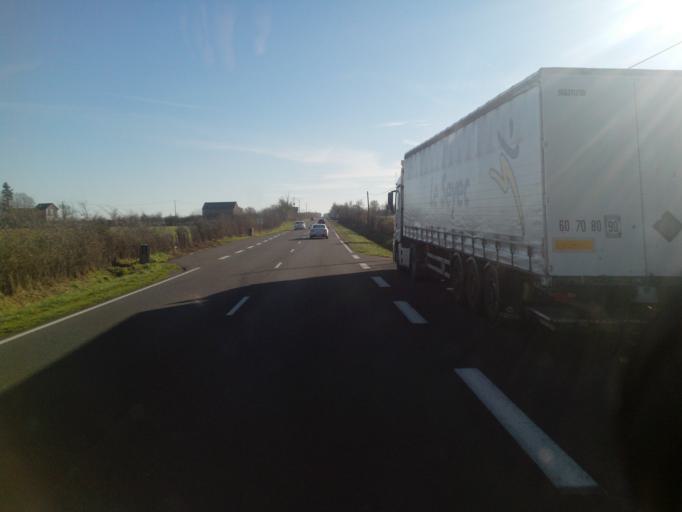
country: FR
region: Poitou-Charentes
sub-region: Departement de la Vienne
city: Lussac-les-Chateaux
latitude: 46.3712
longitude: 0.7628
